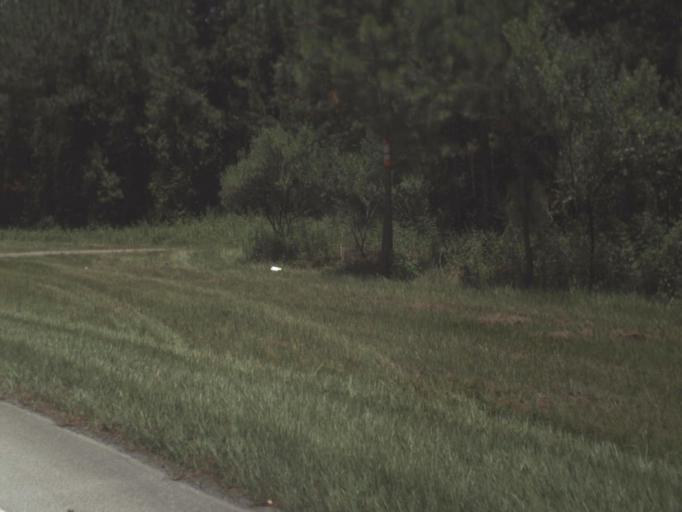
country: US
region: Florida
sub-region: Baker County
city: Macclenny
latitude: 30.1472
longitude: -82.1857
